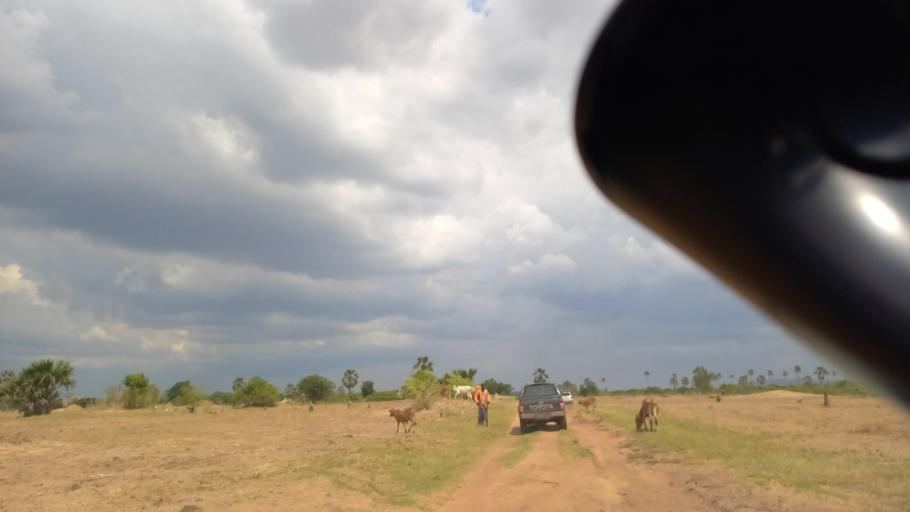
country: ZM
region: Lusaka
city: Kafue
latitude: -15.8309
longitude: 28.0643
